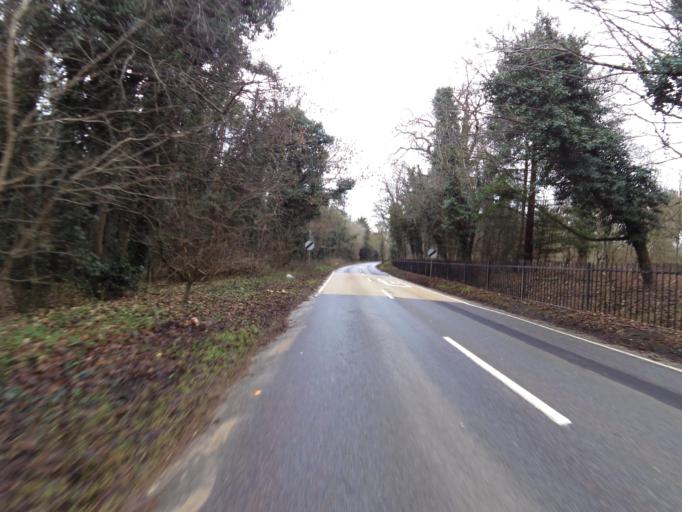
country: GB
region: England
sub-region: Suffolk
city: Bramford
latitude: 52.1236
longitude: 1.1023
